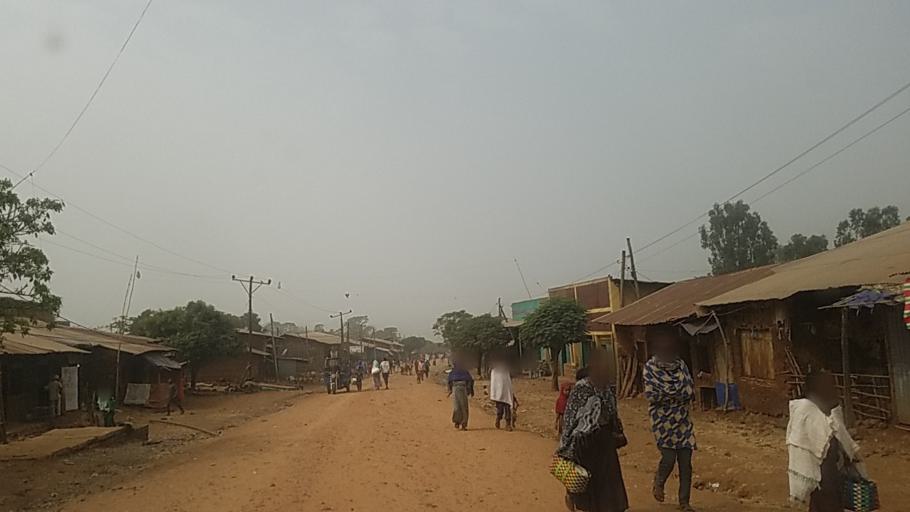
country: ET
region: Amhara
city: Bure
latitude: 10.8482
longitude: 36.3465
